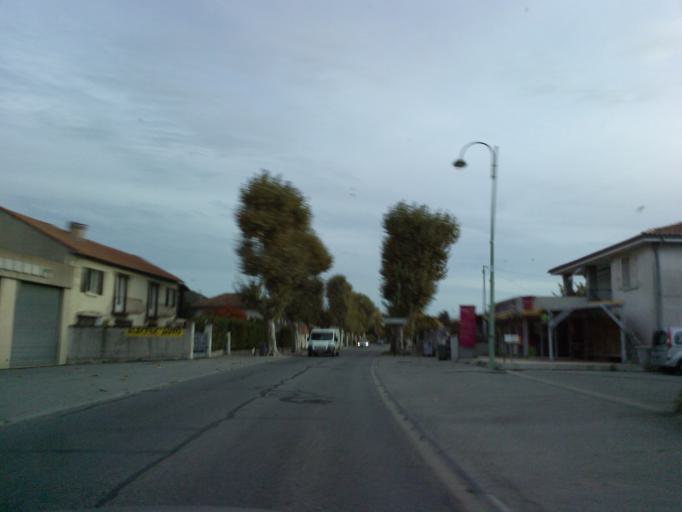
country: FR
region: Provence-Alpes-Cote d'Azur
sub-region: Departement des Alpes-de-Haute-Provence
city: Sisteron
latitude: 44.1845
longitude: 5.9489
